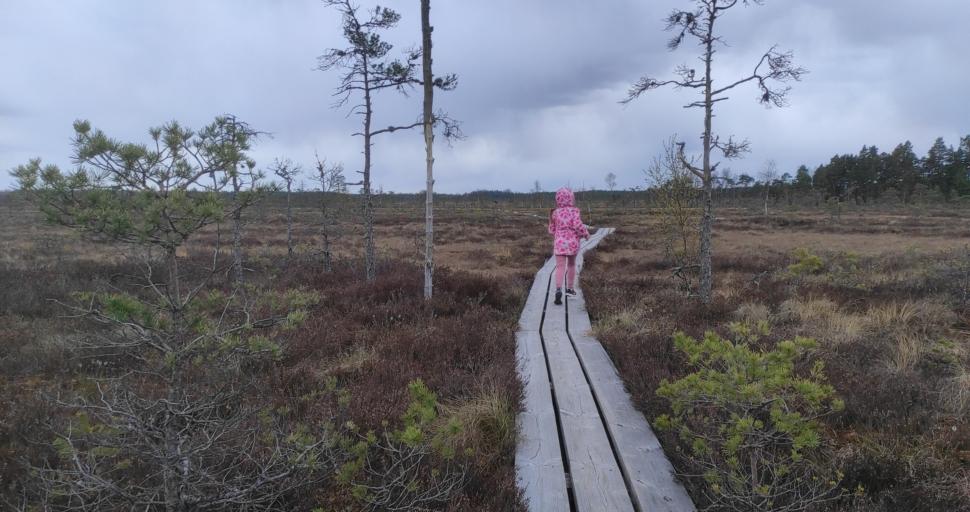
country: LV
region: Dundaga
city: Dundaga
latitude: 57.3462
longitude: 22.1567
